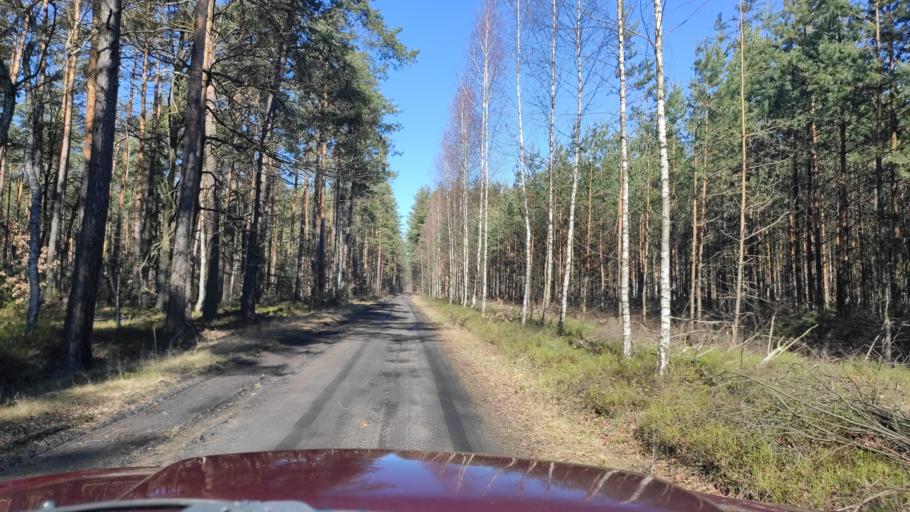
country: PL
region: Masovian Voivodeship
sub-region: Powiat kozienicki
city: Garbatka-Letnisko
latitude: 51.4297
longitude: 21.5486
